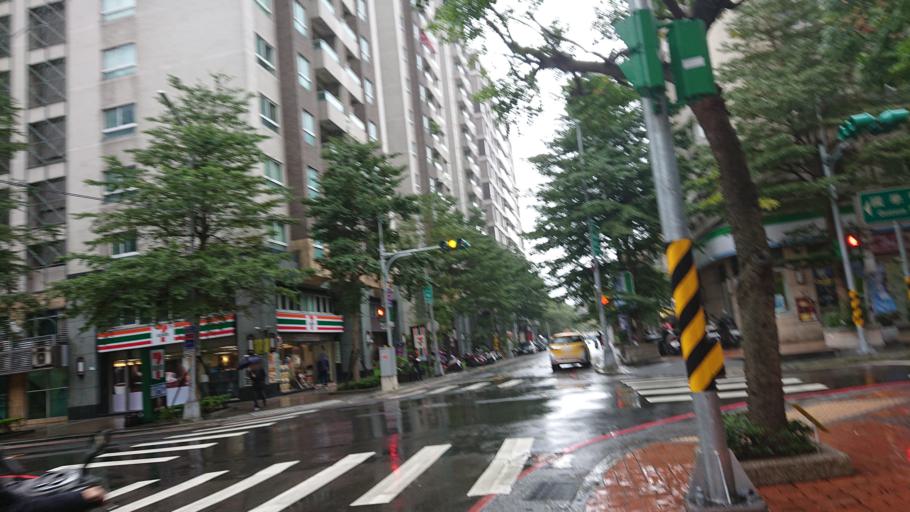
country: TW
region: Taiwan
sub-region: Taoyuan
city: Taoyuan
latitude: 24.9424
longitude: 121.3731
